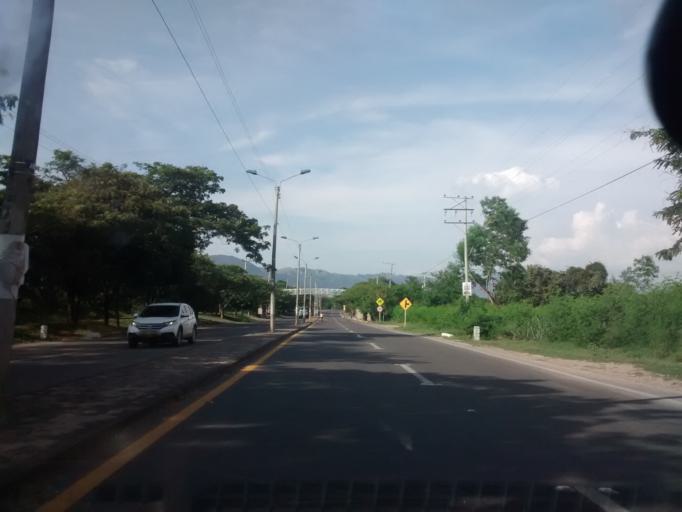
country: CO
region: Cundinamarca
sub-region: Girardot
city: Girardot City
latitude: 4.3133
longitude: -74.8050
